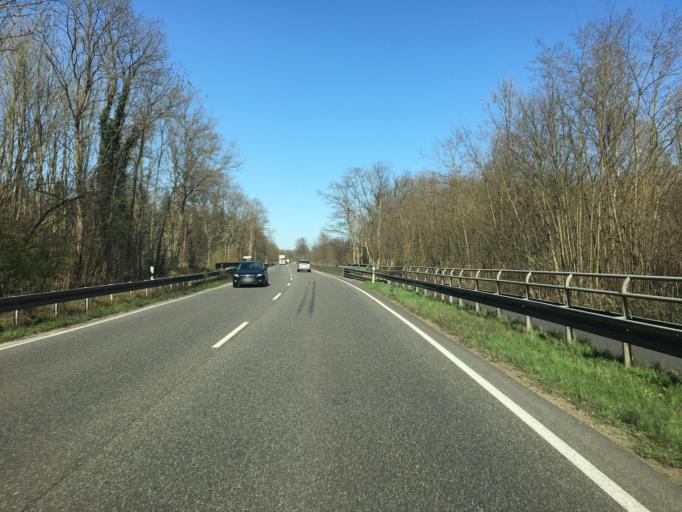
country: DE
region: North Rhine-Westphalia
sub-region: Regierungsbezirk Koln
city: Frechen
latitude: 50.8833
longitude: 6.7898
